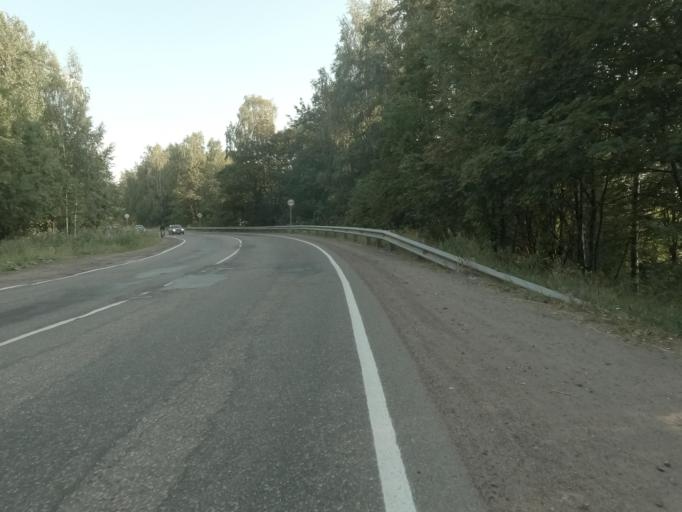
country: RU
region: Leningrad
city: Vyborg
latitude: 60.7284
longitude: 28.7596
